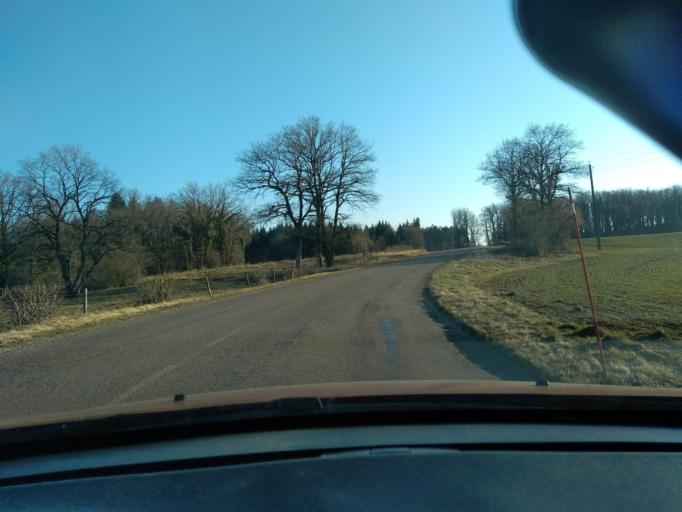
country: FR
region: Franche-Comte
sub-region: Departement du Jura
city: Perrigny
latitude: 46.6557
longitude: 5.6446
